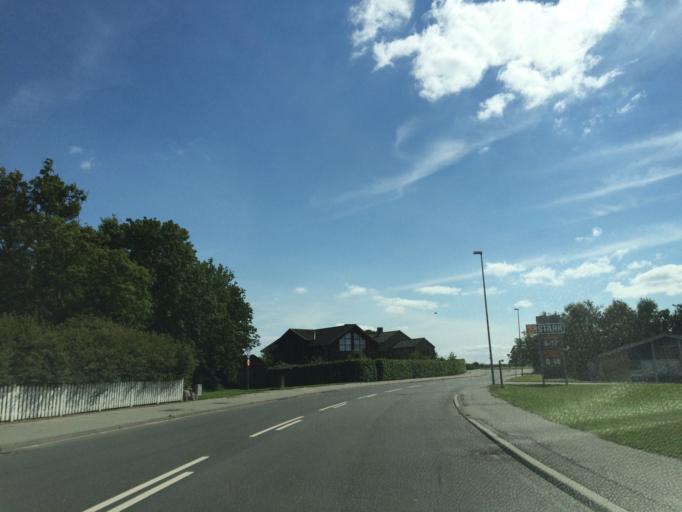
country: DK
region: Central Jutland
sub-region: Syddjurs Kommune
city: Ronde
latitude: 56.3019
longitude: 10.4653
